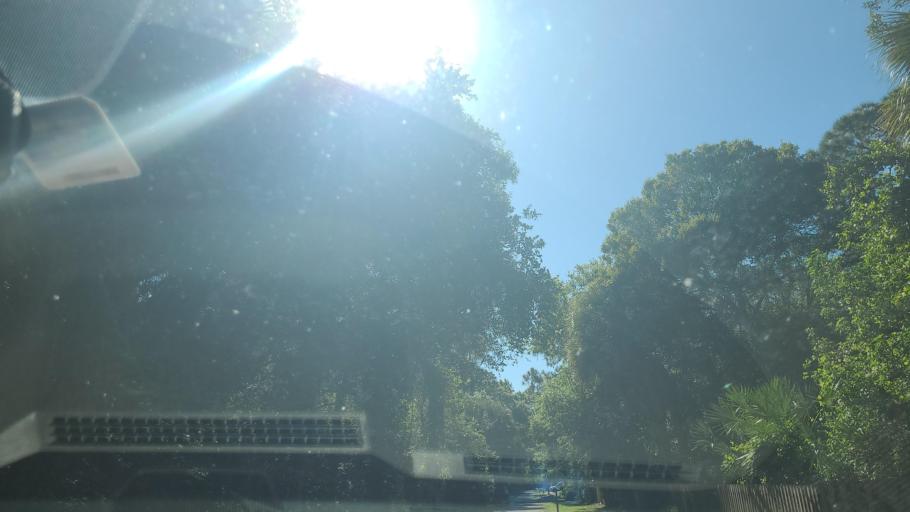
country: US
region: Florida
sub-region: Indian River County
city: Sebastian
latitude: 27.7544
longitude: -80.4786
